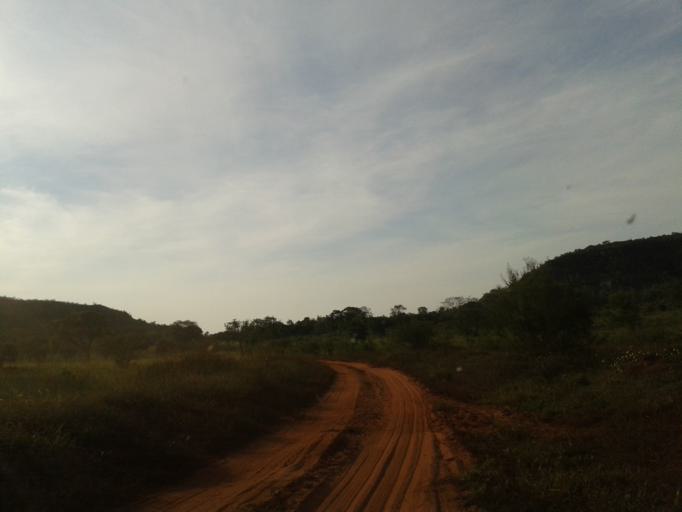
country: BR
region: Minas Gerais
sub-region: Campina Verde
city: Campina Verde
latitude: -19.5023
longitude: -49.6046
